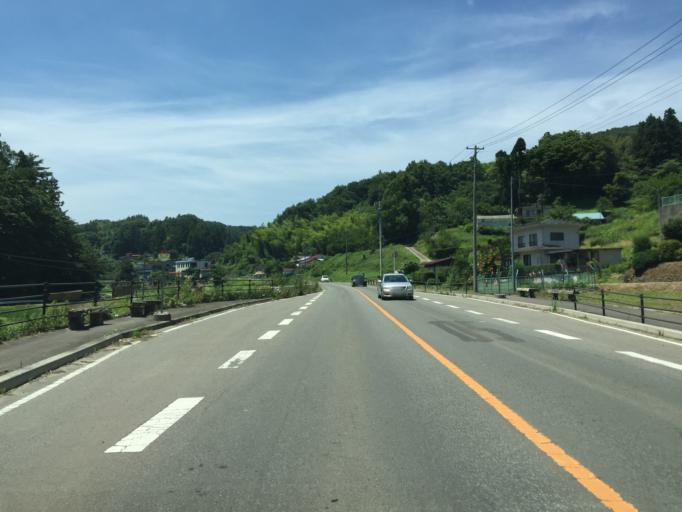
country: JP
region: Fukushima
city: Hobaramachi
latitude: 37.7564
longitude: 140.5499
